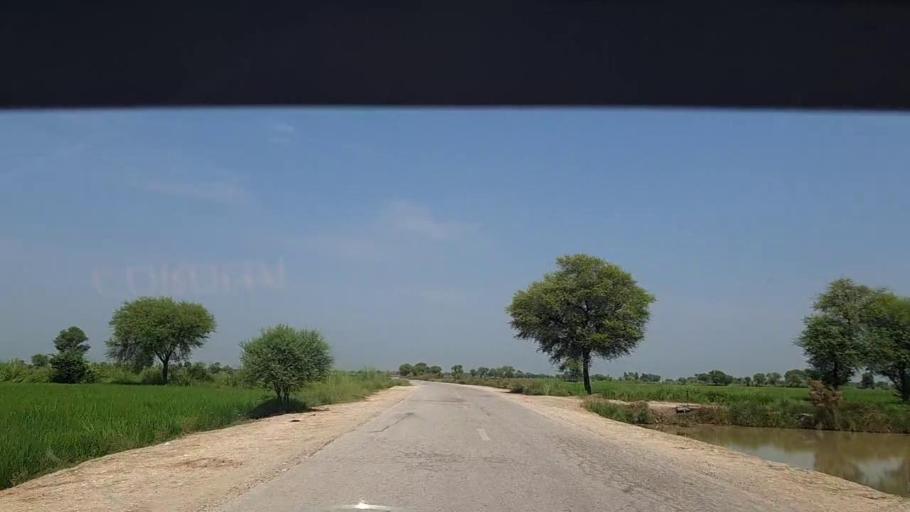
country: PK
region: Sindh
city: Thul
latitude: 28.1312
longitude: 68.8179
